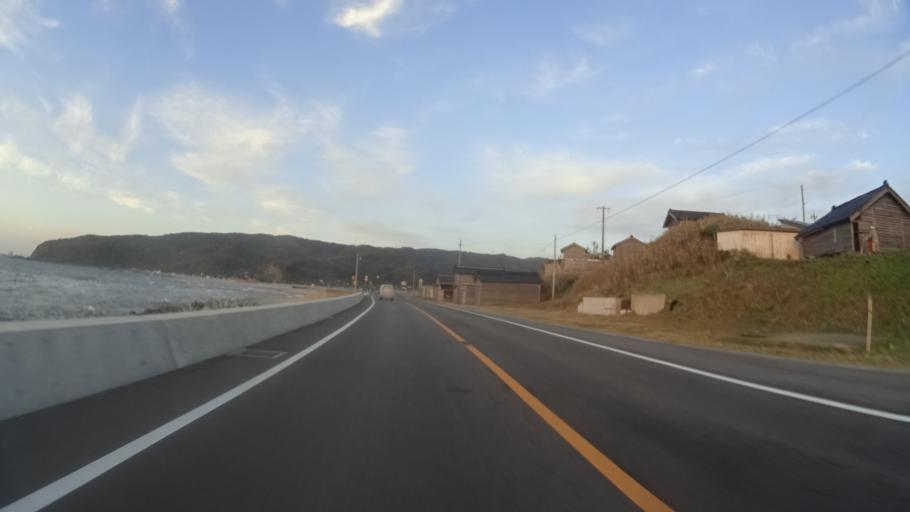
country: JP
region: Ishikawa
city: Nanao
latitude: 37.2837
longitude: 136.7350
